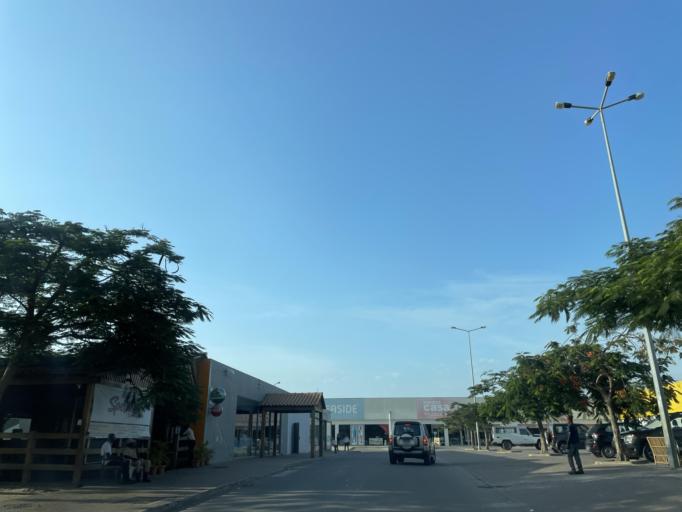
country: AO
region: Luanda
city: Luanda
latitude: -8.9044
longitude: 13.2353
